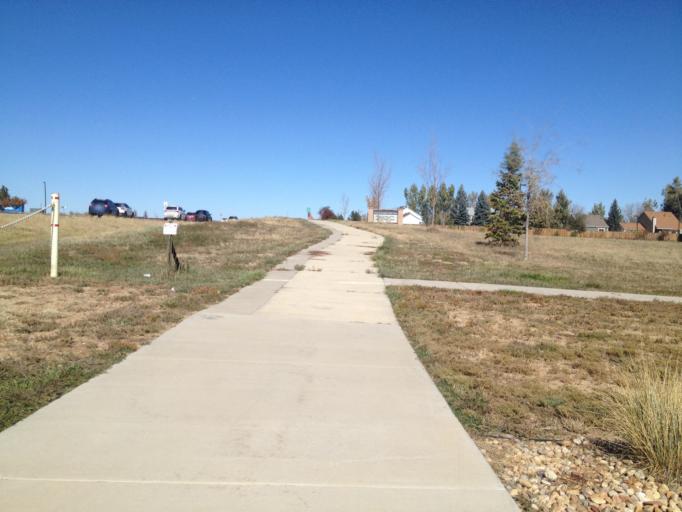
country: US
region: Colorado
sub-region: Boulder County
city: Lafayette
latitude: 40.0060
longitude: -105.1026
